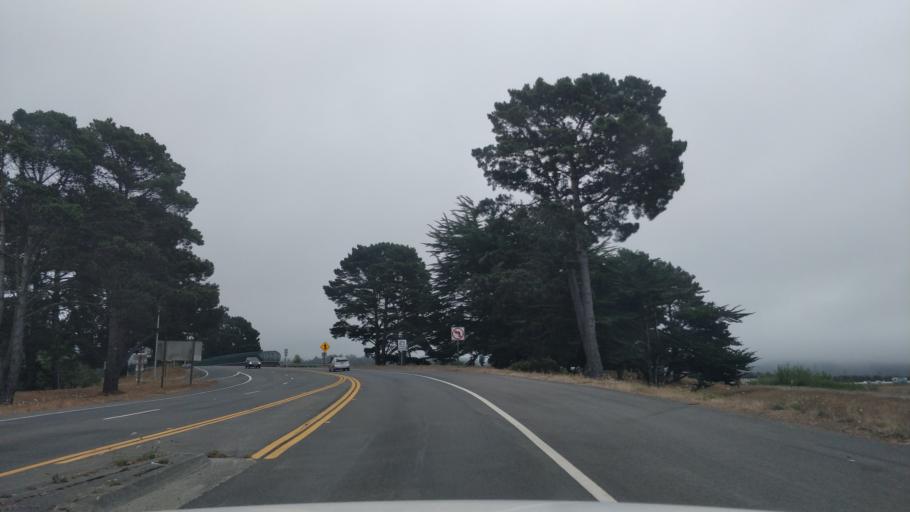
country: US
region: California
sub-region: Humboldt County
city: Arcata
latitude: 40.8634
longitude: -124.0849
